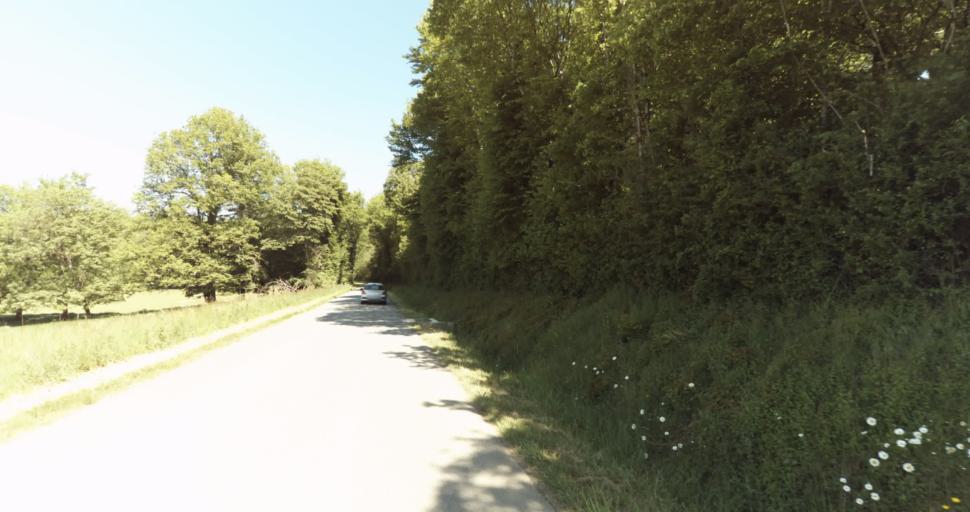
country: FR
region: Limousin
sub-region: Departement de la Haute-Vienne
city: Le Vigen
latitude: 45.7475
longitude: 1.3075
